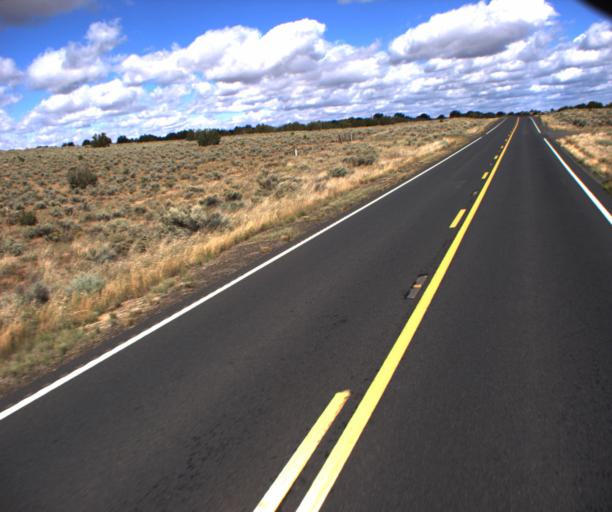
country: US
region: Arizona
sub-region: Apache County
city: Houck
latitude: 35.1647
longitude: -109.3375
